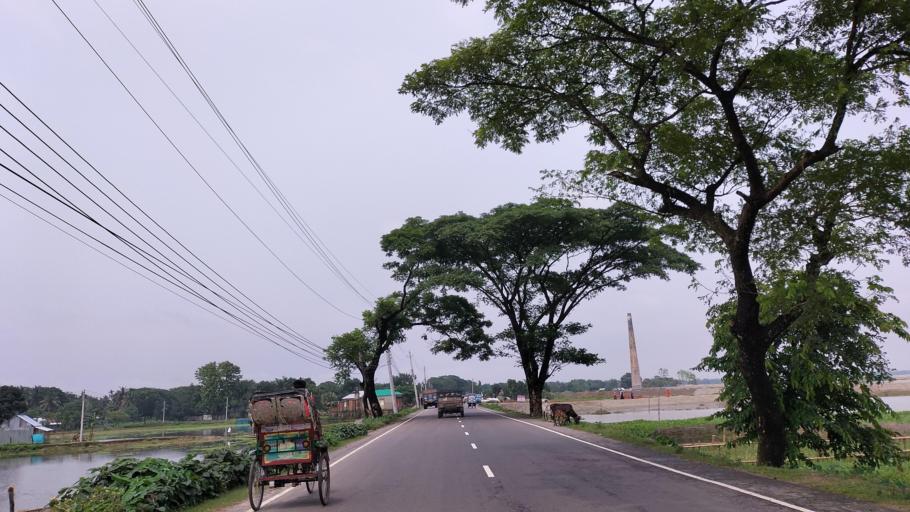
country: BD
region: Dhaka
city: Netrakona
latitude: 24.8986
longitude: 90.7497
